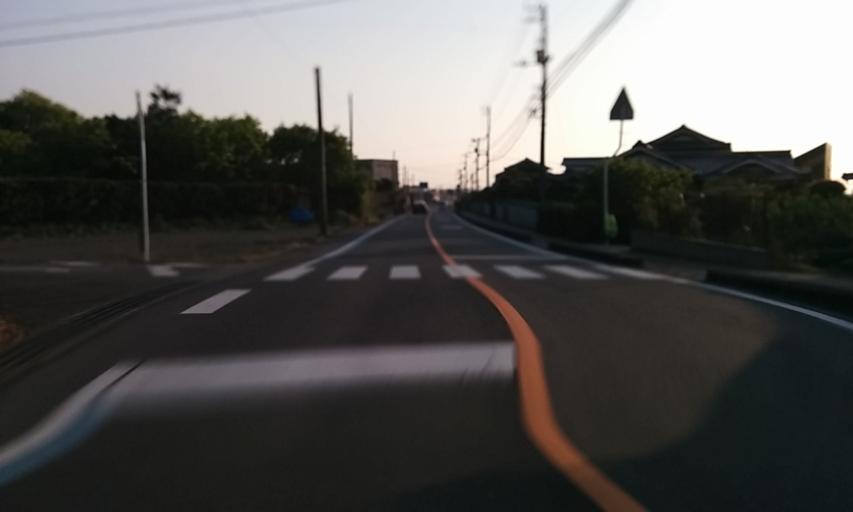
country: JP
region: Ehime
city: Masaki-cho
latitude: 33.7765
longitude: 132.7519
